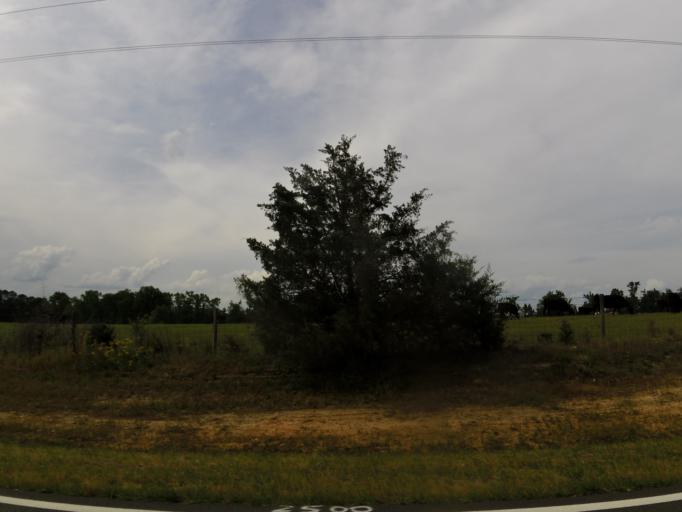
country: US
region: Georgia
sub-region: McDuffie County
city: Thomson
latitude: 33.5232
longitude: -82.4489
